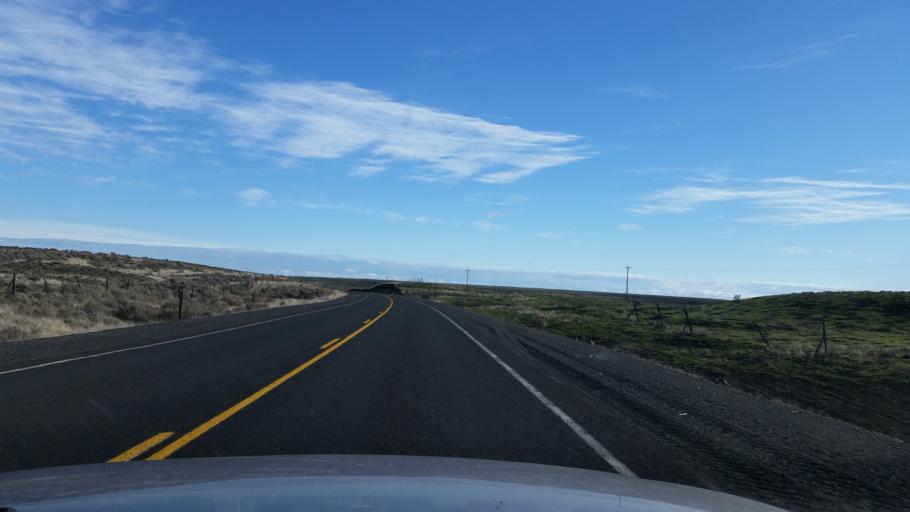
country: US
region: Washington
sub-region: Grant County
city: Warden
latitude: 47.3197
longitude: -118.8582
